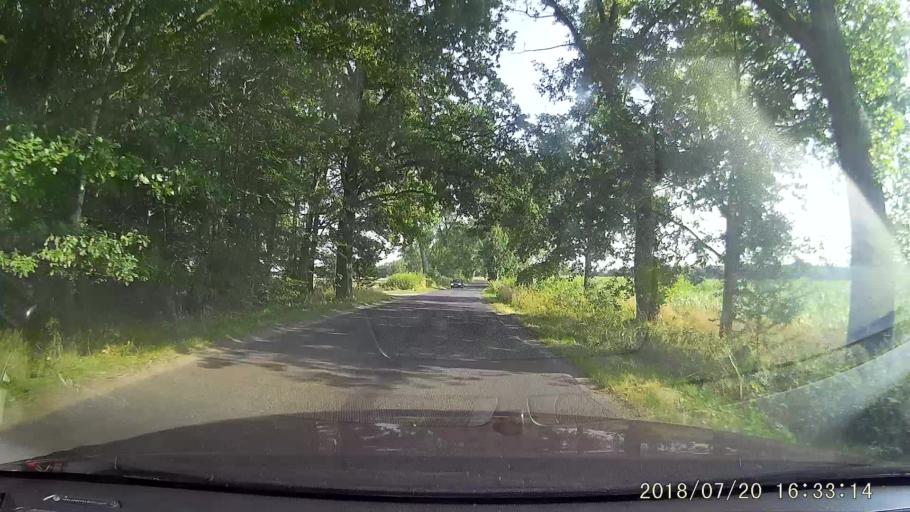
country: PL
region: Lower Silesian Voivodeship
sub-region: Powiat zgorzelecki
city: Sulikow
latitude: 51.0918
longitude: 15.0954
